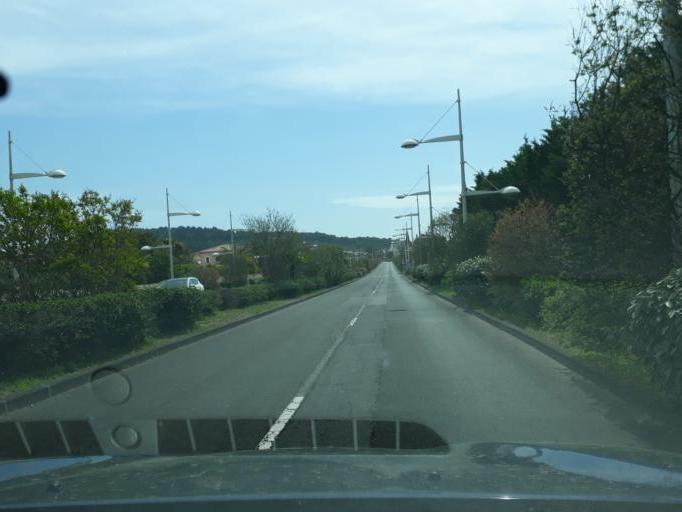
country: FR
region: Languedoc-Roussillon
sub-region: Departement de l'Herault
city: Agde
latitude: 43.3021
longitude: 3.4876
